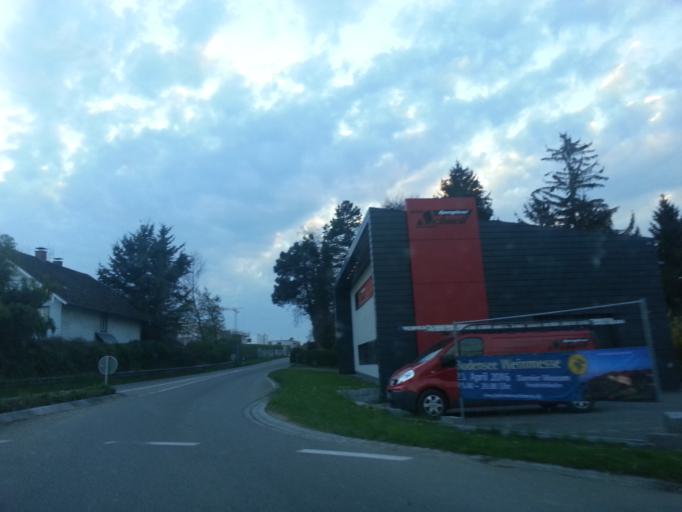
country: DE
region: Bavaria
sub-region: Swabia
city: Bodolz
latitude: 47.5718
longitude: 9.6445
